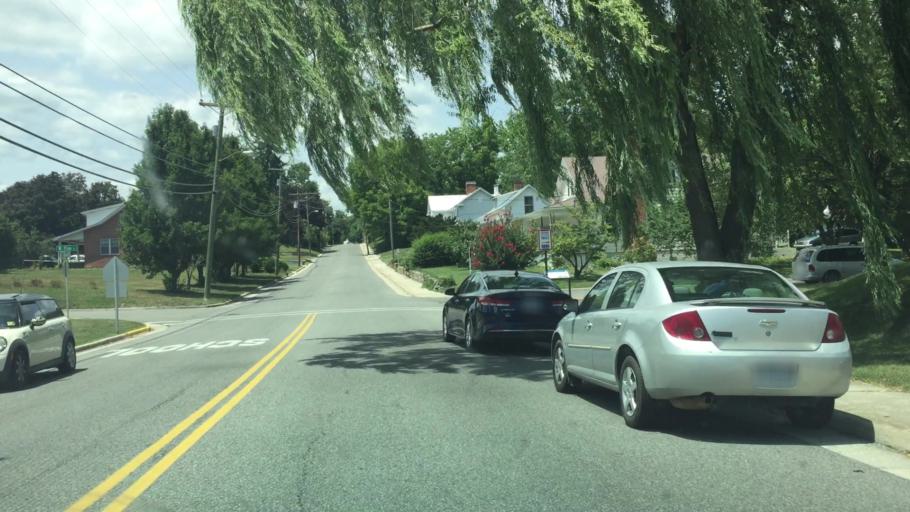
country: US
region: Virginia
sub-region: Wythe County
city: Wytheville
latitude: 36.9523
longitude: -81.0863
